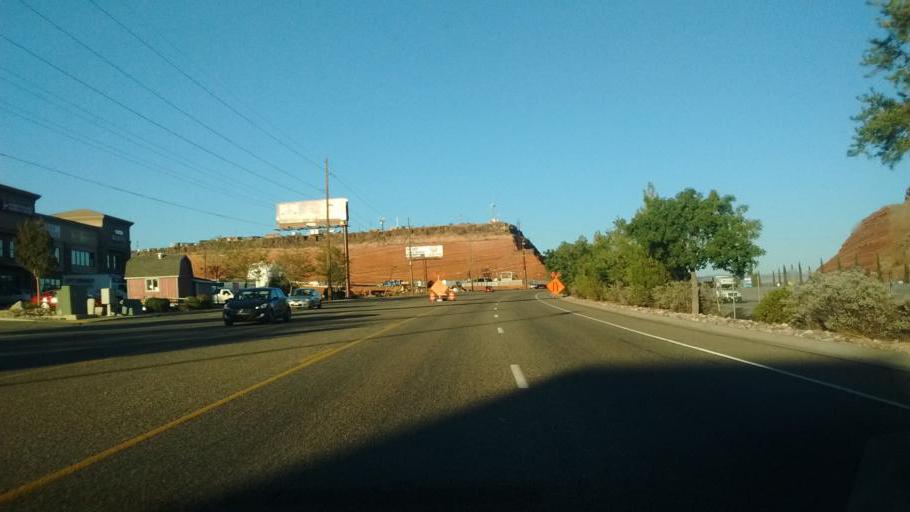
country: US
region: Utah
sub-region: Washington County
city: Saint George
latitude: 37.1144
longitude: -113.5554
